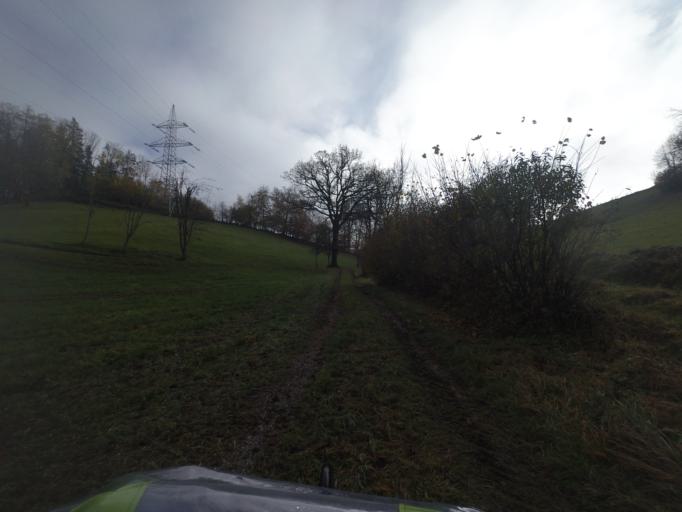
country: AT
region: Salzburg
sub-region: Politischer Bezirk Hallein
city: Adnet
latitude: 47.6757
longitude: 13.1445
